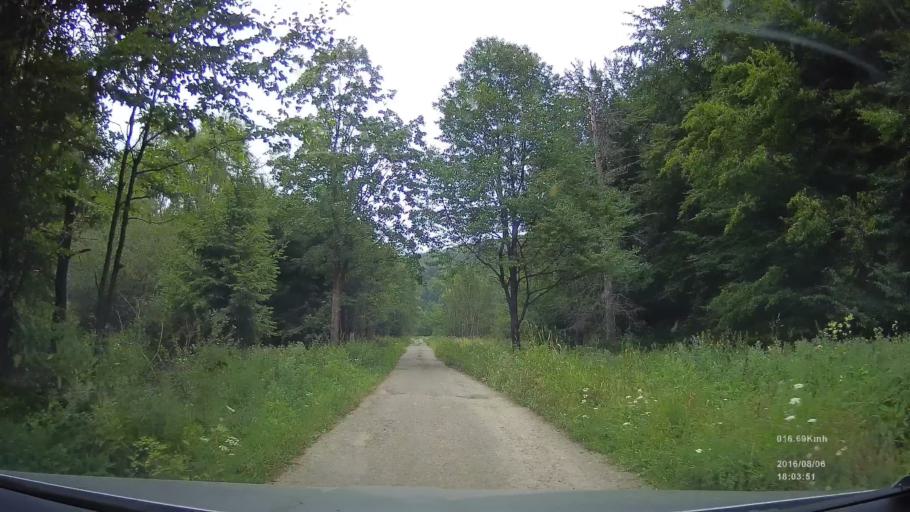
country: SK
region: Presovsky
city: Svidnik
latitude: 49.4109
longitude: 21.5700
